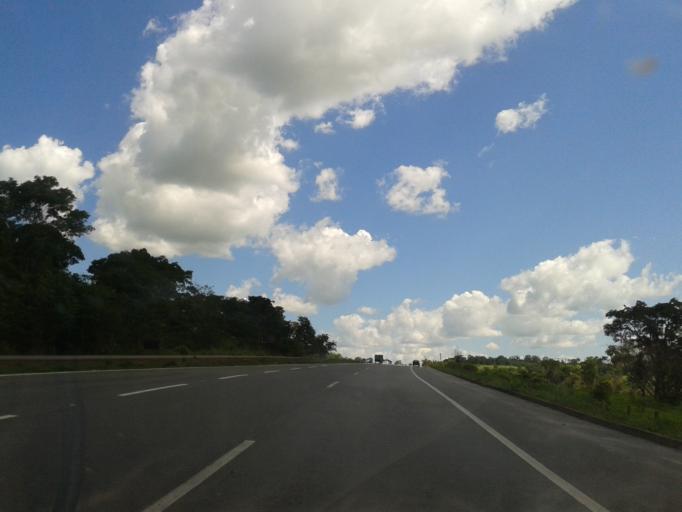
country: BR
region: Goias
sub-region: Pontalina
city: Pontalina
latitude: -17.4688
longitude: -49.2179
